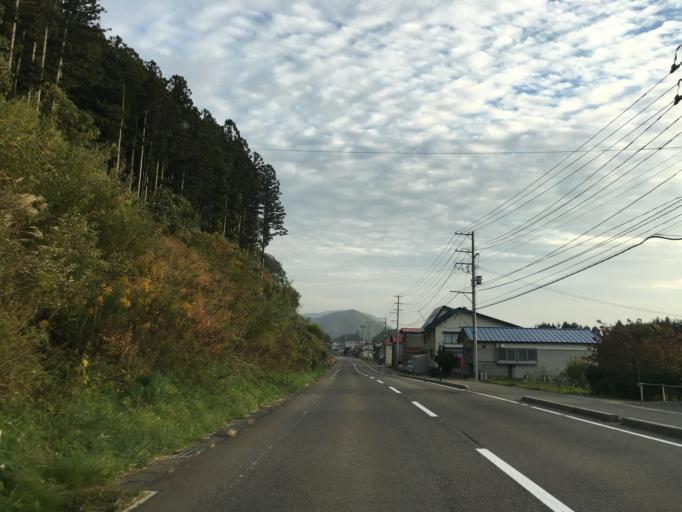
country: JP
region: Fukushima
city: Inawashiro
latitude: 37.5171
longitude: 140.1440
